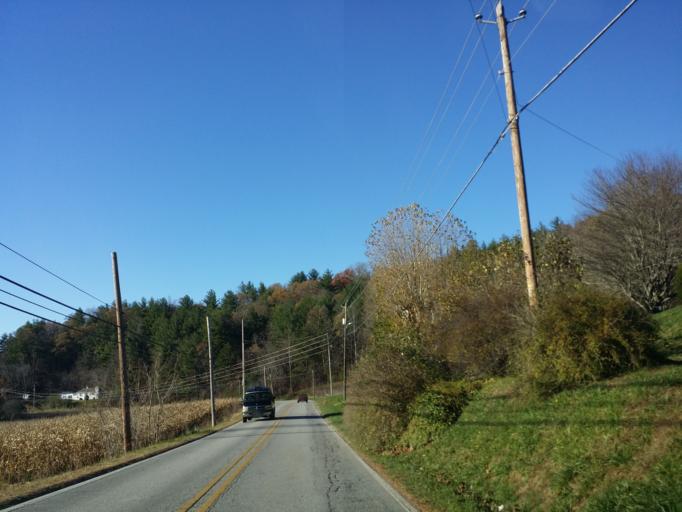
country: US
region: North Carolina
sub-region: Buncombe County
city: Swannanoa
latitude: 35.6102
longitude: -82.4149
